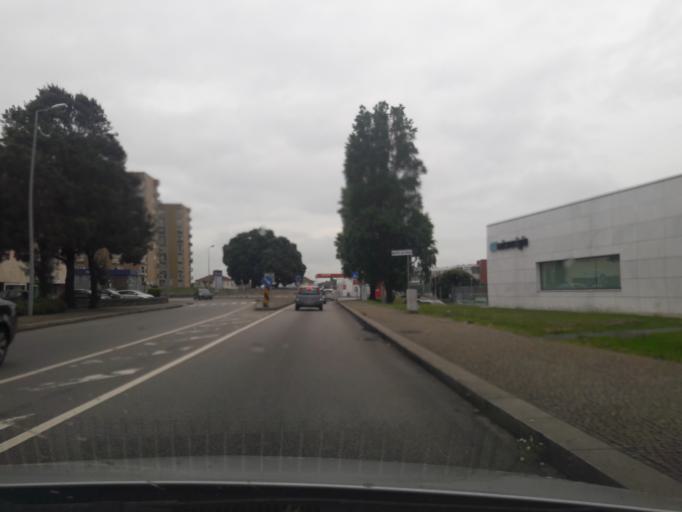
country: PT
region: Porto
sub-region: Vila do Conde
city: Vila do Conde
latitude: 41.3424
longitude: -8.7351
